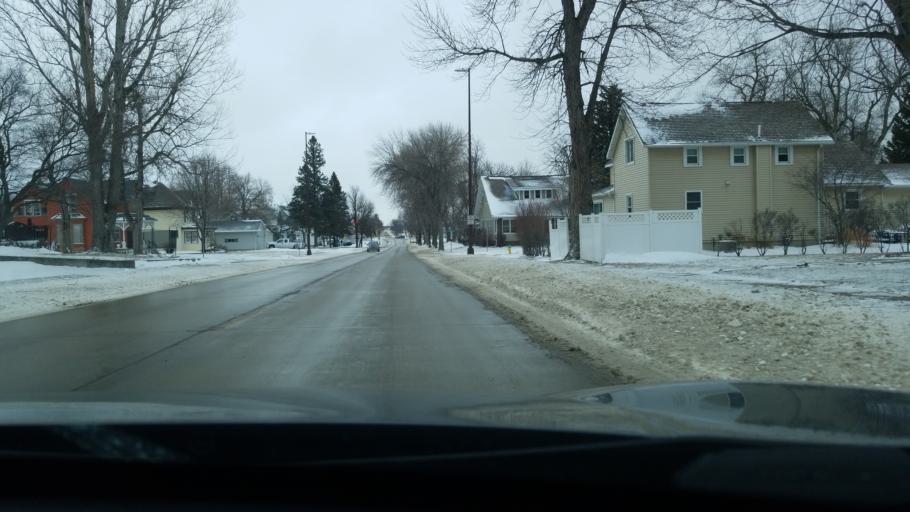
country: US
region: Iowa
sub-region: Lyon County
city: Rock Rapids
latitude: 43.4280
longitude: -96.1756
